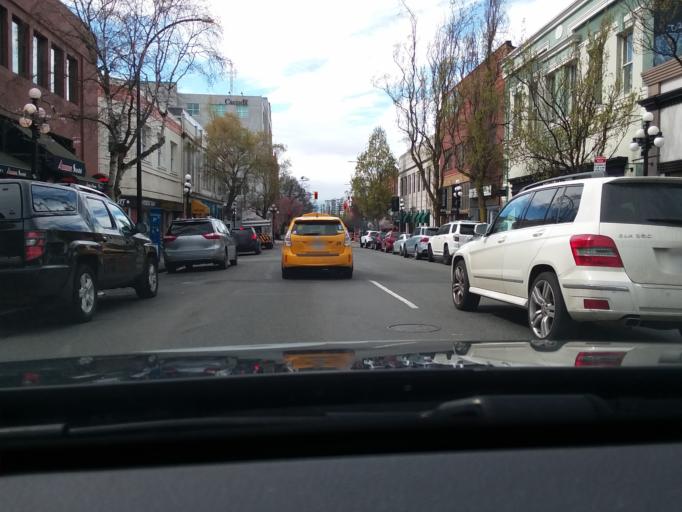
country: CA
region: British Columbia
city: Victoria
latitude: 48.4265
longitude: -123.3664
